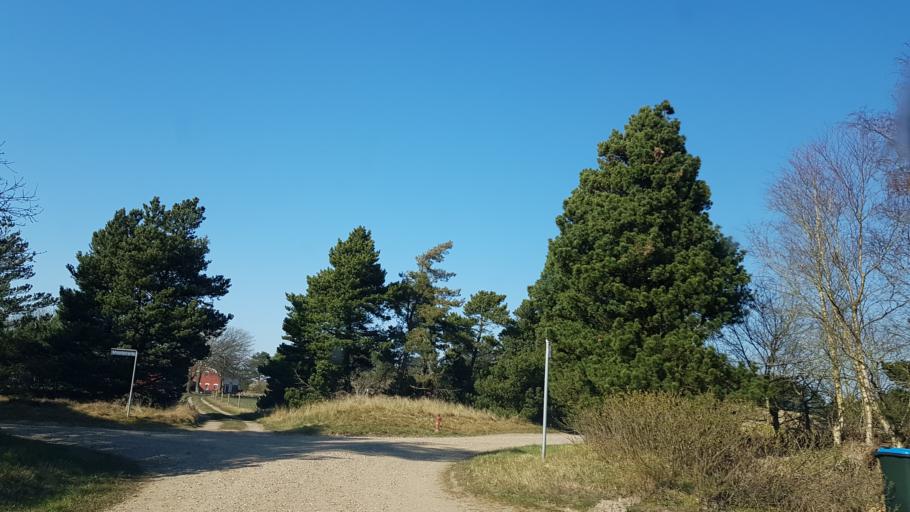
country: DE
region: Schleswig-Holstein
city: List
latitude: 55.1004
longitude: 8.5343
